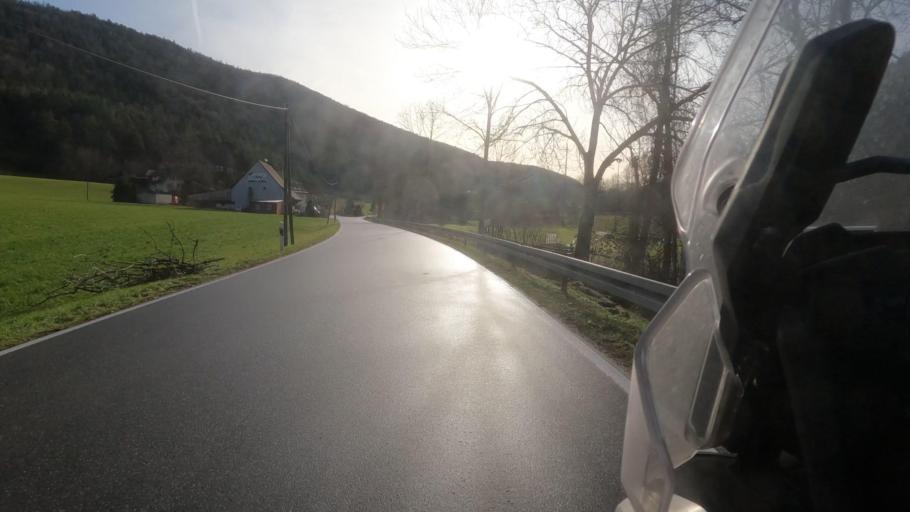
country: DE
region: Baden-Wuerttemberg
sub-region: Freiburg Region
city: Tengen
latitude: 47.7816
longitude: 8.6177
